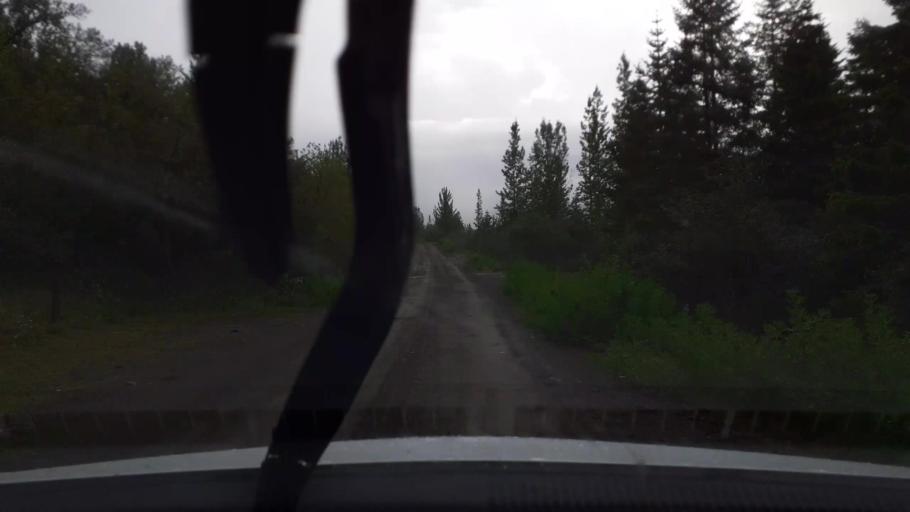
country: IS
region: Capital Region
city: Mosfellsbaer
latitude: 64.4925
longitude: -21.3432
